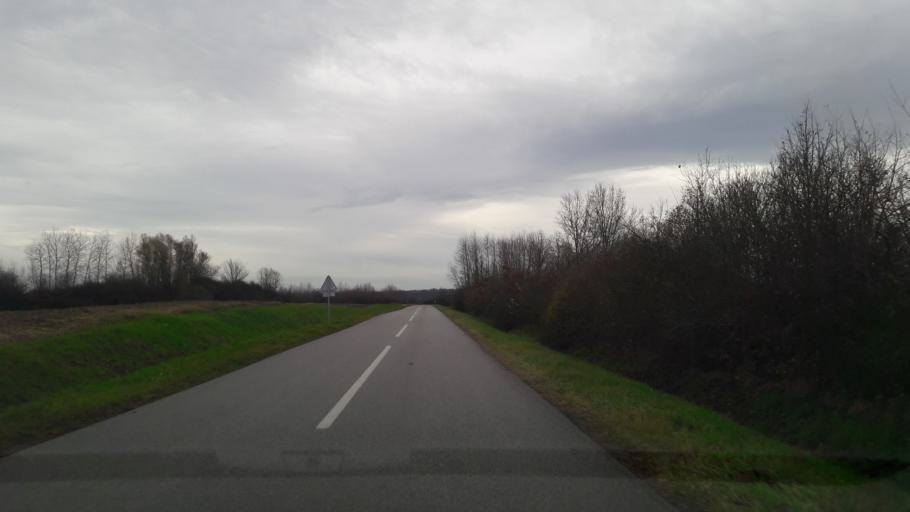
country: HR
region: Osjecko-Baranjska
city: Velimirovac
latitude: 45.6351
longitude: 18.1081
